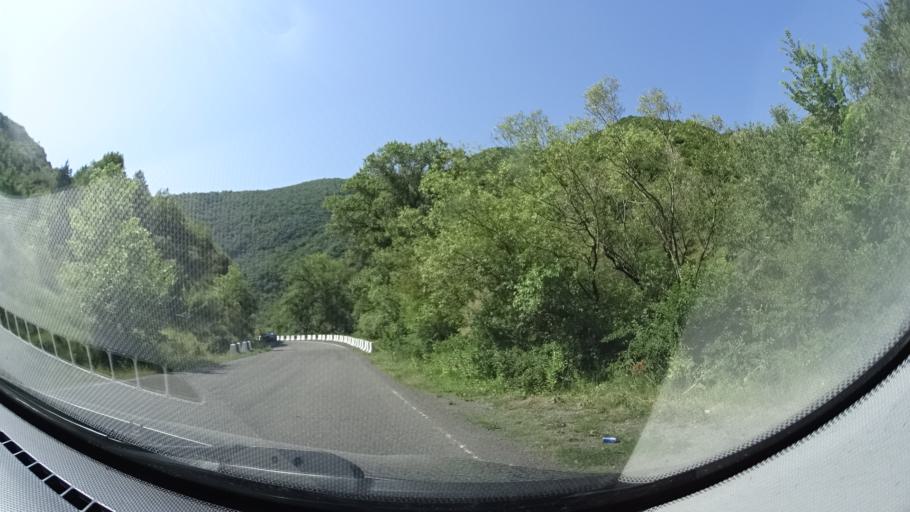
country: GE
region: Samtskhe-Javakheti
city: Akhaltsikhe
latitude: 41.6126
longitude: 43.0653
